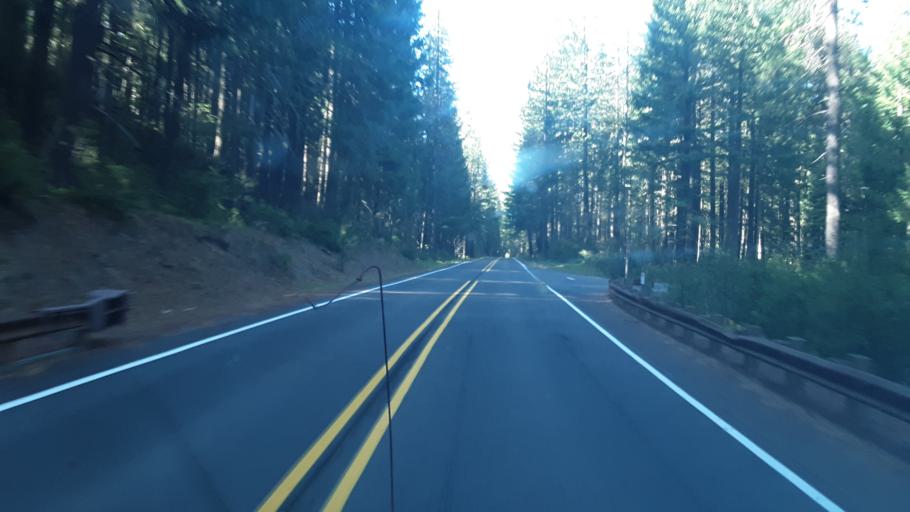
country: US
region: Oregon
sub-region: Jackson County
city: Shady Cove
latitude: 42.9333
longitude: -122.4217
